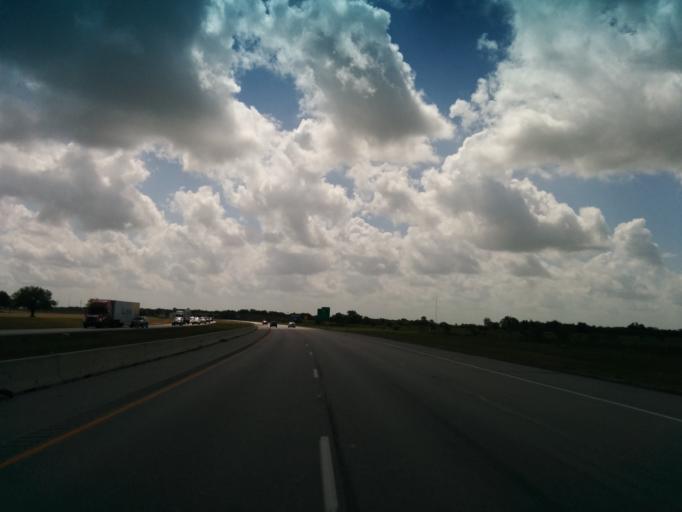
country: US
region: Texas
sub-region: Austin County
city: Sealy
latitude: 29.7604
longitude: -96.1768
